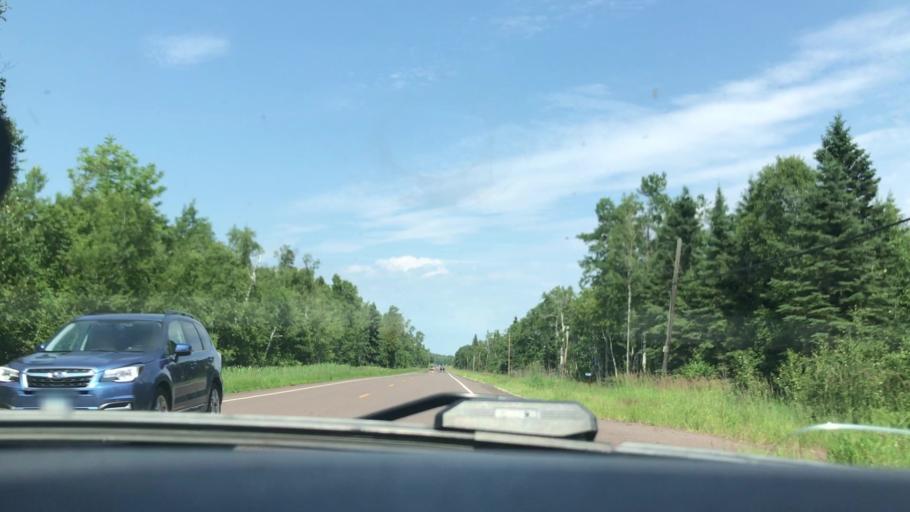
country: US
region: Minnesota
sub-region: Cook County
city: Grand Marais
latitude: 47.6326
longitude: -90.7219
